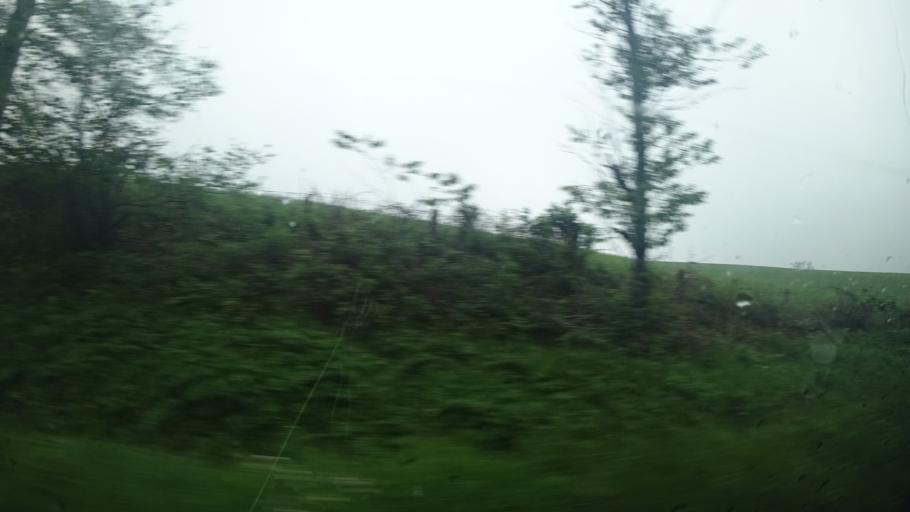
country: FR
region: Midi-Pyrenees
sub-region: Departement de l'Aveyron
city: Laissac
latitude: 44.3245
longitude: 2.7886
